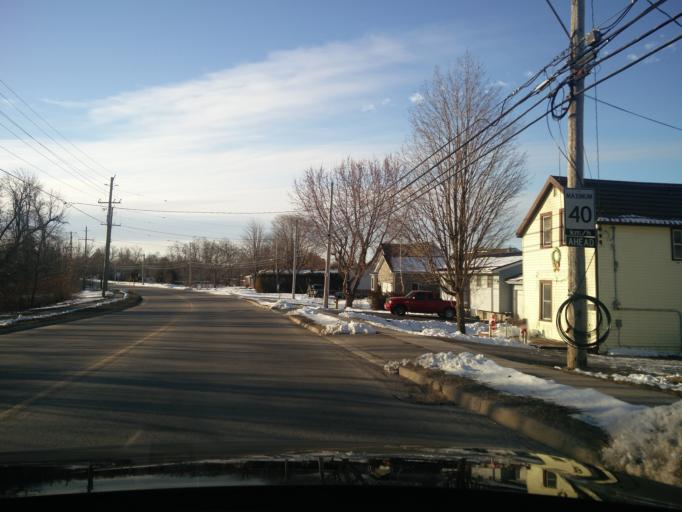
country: CA
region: Ontario
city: Gananoque
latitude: 44.3360
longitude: -76.1690
